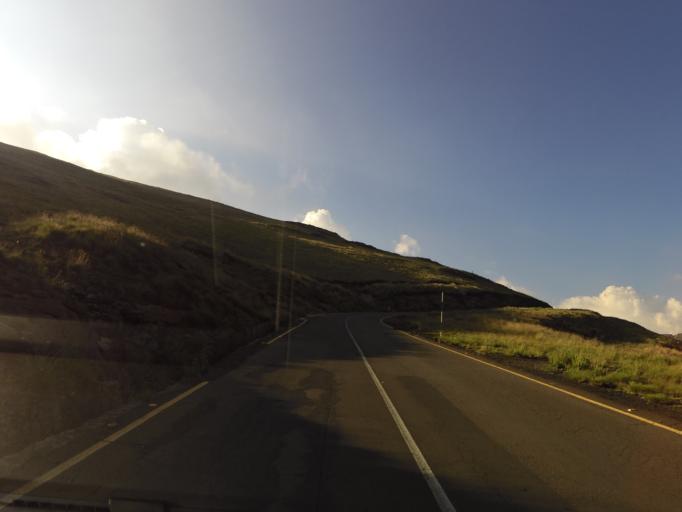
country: LS
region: Butha-Buthe
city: Butha-Buthe
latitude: -29.0764
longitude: 28.4253
